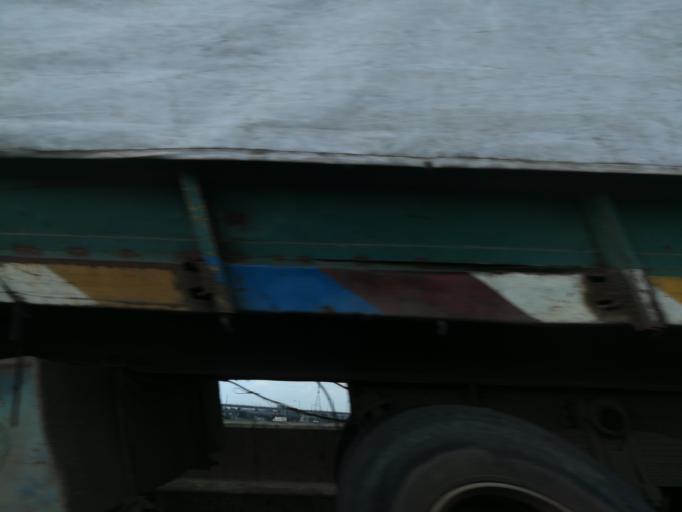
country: NG
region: Lagos
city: Ebute Metta
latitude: 6.4819
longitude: 3.3673
